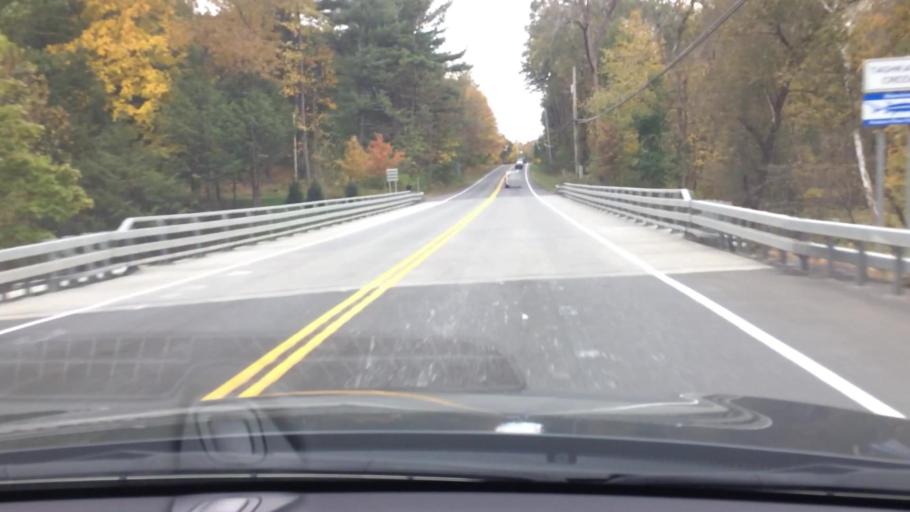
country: US
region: New York
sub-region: Columbia County
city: Oakdale
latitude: 42.1919
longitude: -73.7531
